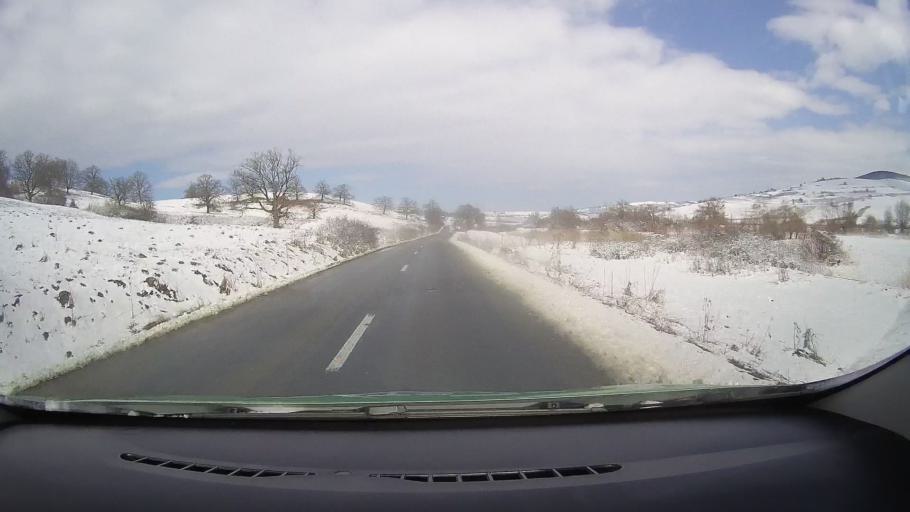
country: RO
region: Sibiu
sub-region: Comuna Altina
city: Altina
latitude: 45.9498
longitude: 24.4516
